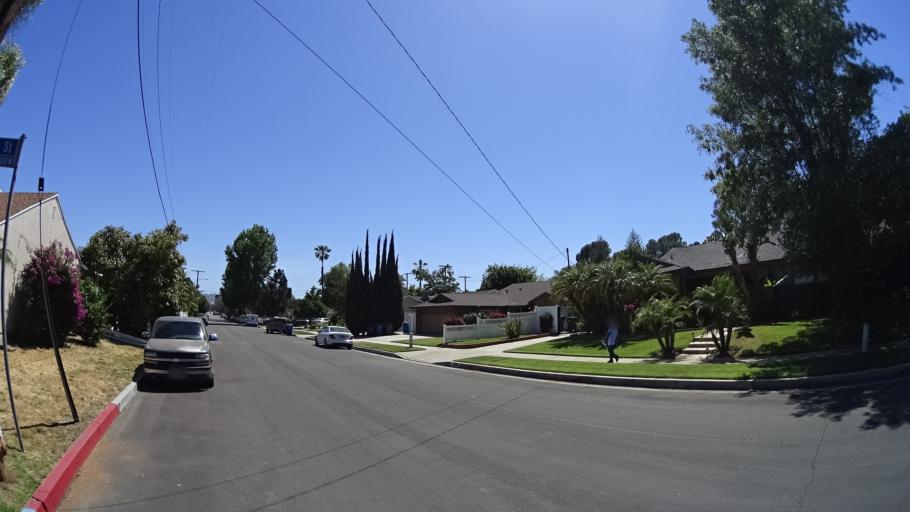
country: US
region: California
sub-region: Los Angeles County
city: North Hollywood
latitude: 34.1744
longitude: -118.4020
